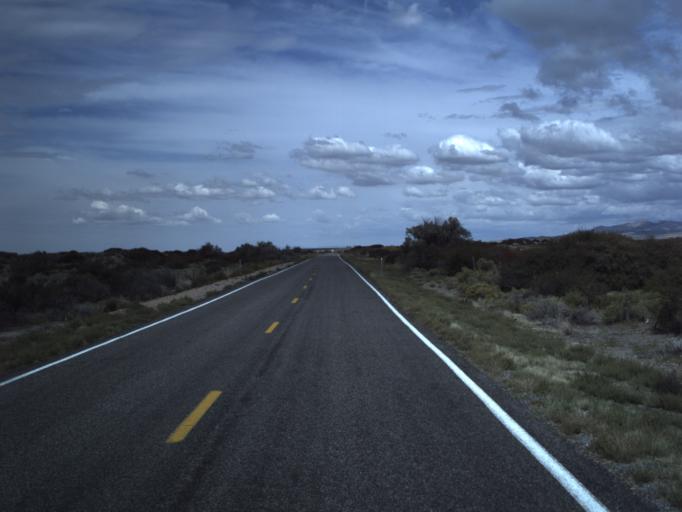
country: US
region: Utah
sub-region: Millard County
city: Fillmore
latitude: 39.1197
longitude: -112.4093
